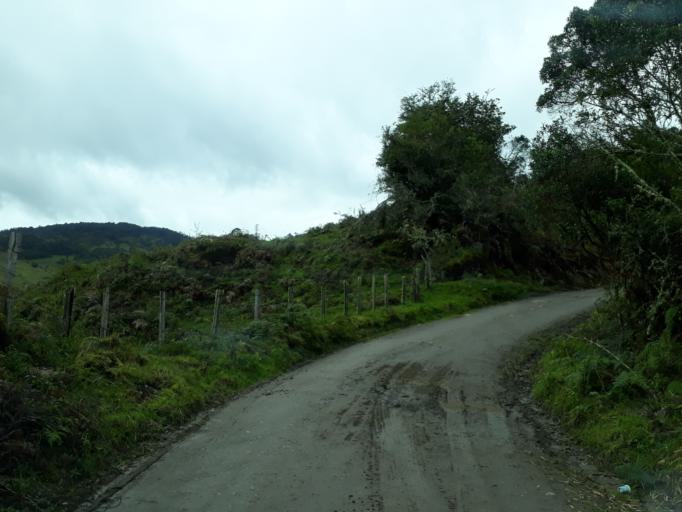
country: CO
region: Cundinamarca
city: Junin
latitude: 4.6901
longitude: -73.6748
